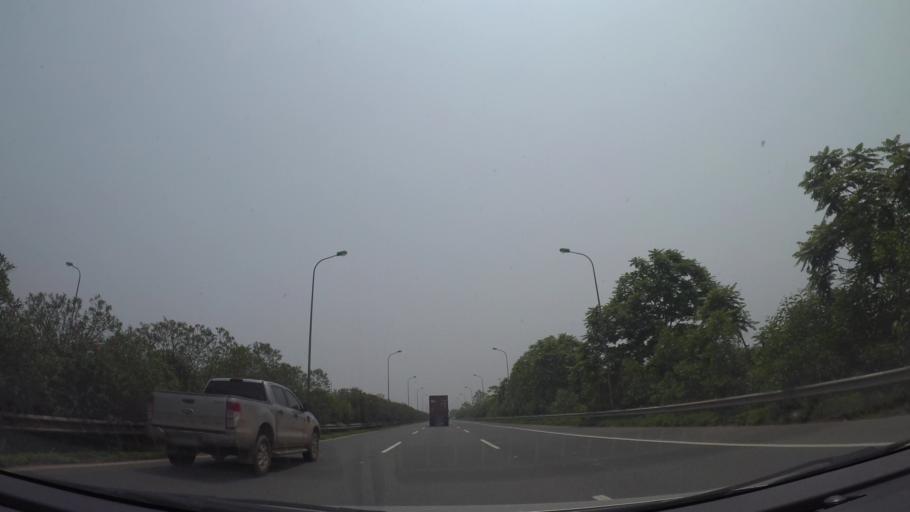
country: VN
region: Ha Noi
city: Quoc Oai
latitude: 21.0035
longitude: 105.6709
